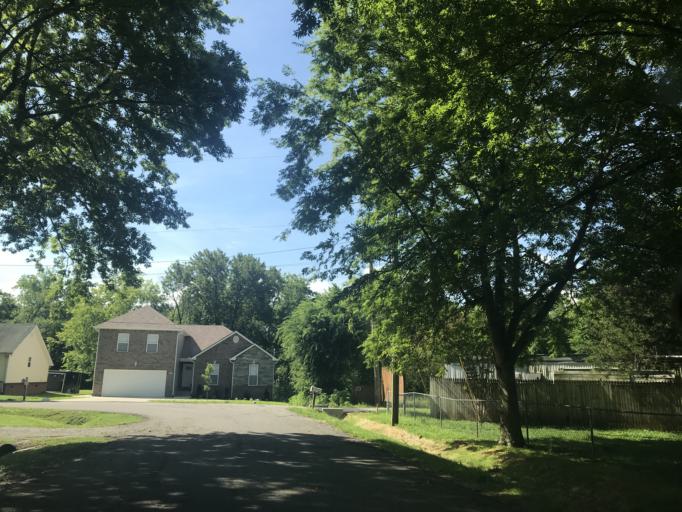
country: US
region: Tennessee
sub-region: Davidson County
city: Nashville
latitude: 36.1913
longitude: -86.8435
